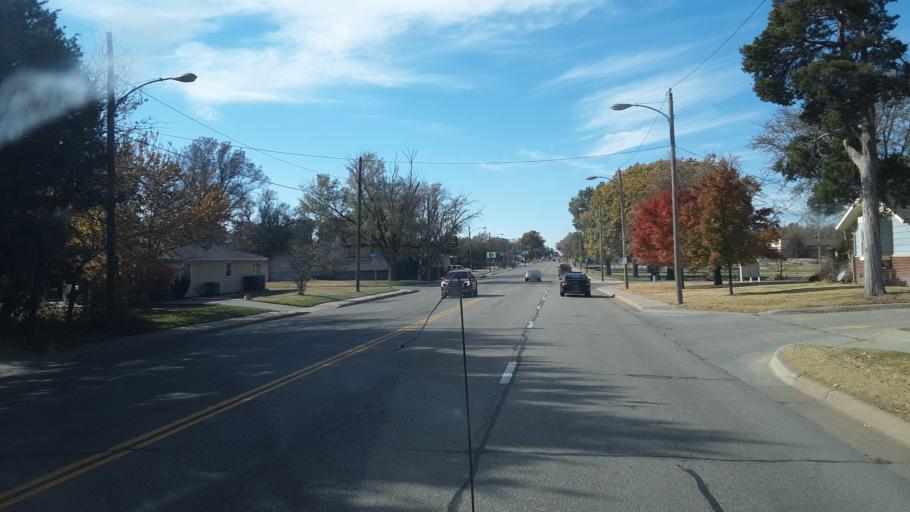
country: US
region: Kansas
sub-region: McPherson County
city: McPherson
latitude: 38.3695
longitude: -97.6505
